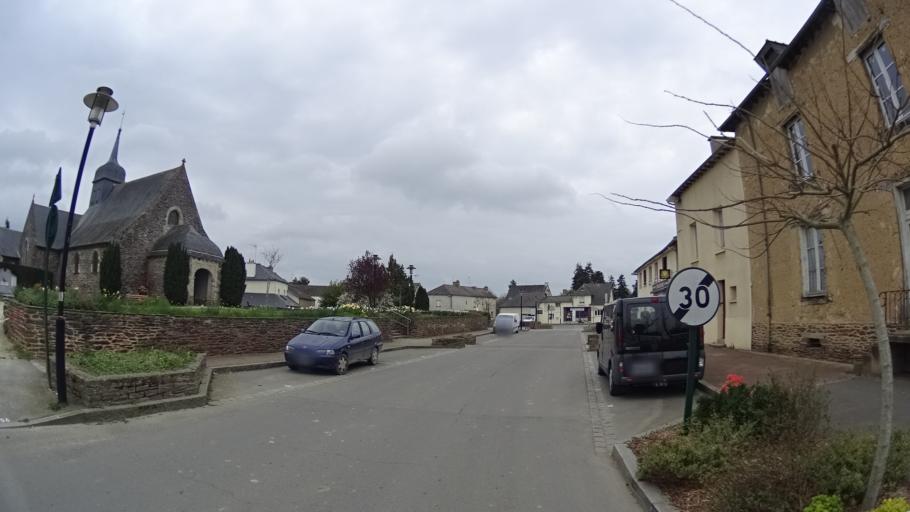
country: FR
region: Brittany
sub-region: Departement d'Ille-et-Vilaine
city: Cintre
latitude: 48.1063
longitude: -1.8718
